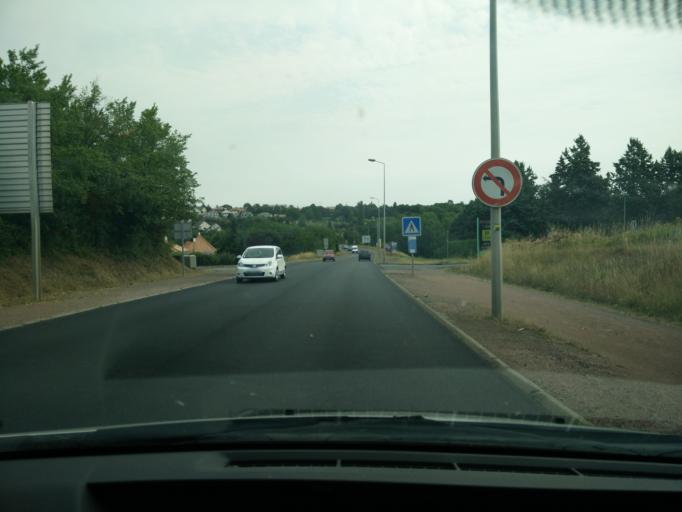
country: FR
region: Poitou-Charentes
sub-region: Departement des Deux-Sevres
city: Saint-Jean-de-Thouars
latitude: 46.9705
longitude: -0.2079
